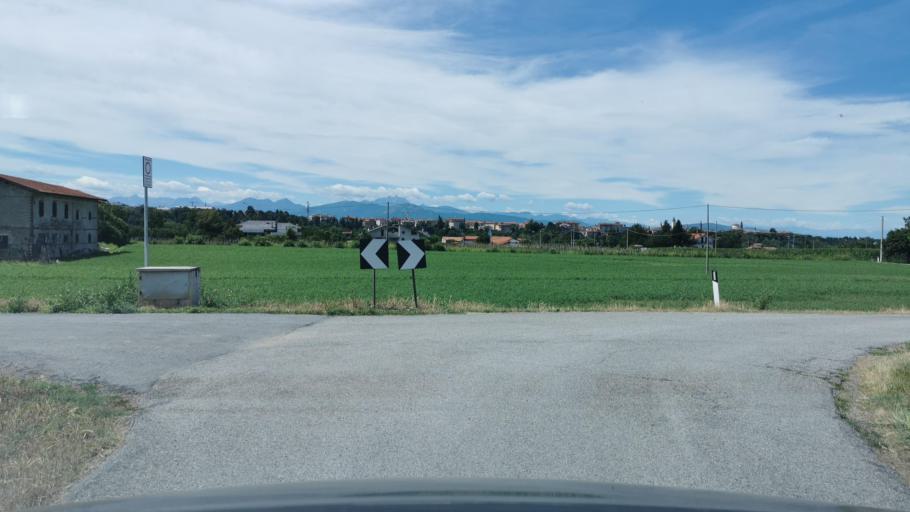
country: IT
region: Piedmont
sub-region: Provincia di Cuneo
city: Cuneo
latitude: 44.3789
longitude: 7.5621
